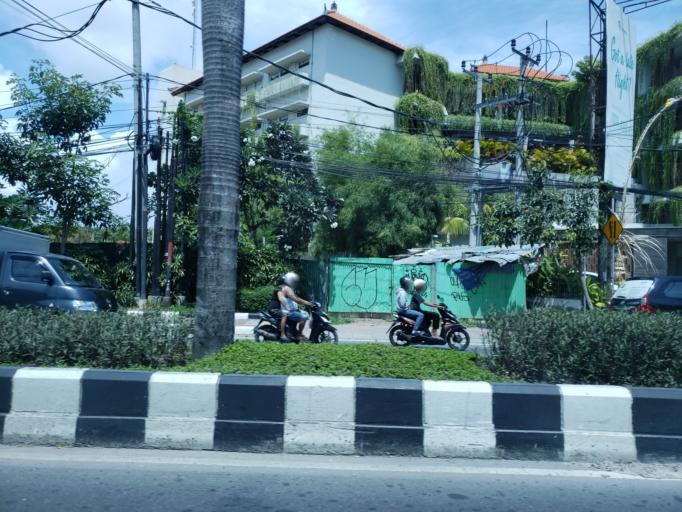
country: ID
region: Bali
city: Kelanabian
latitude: -8.7419
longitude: 115.1811
